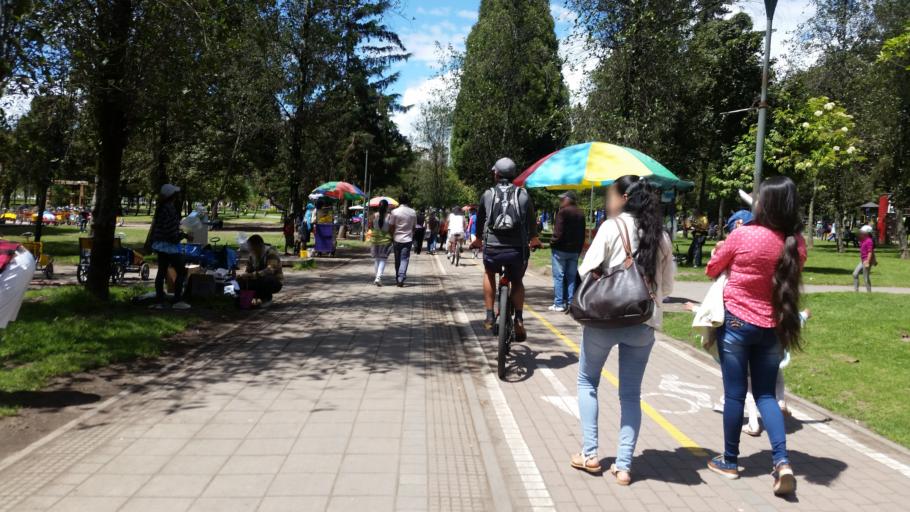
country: EC
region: Pichincha
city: Quito
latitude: -0.2087
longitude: -78.4990
